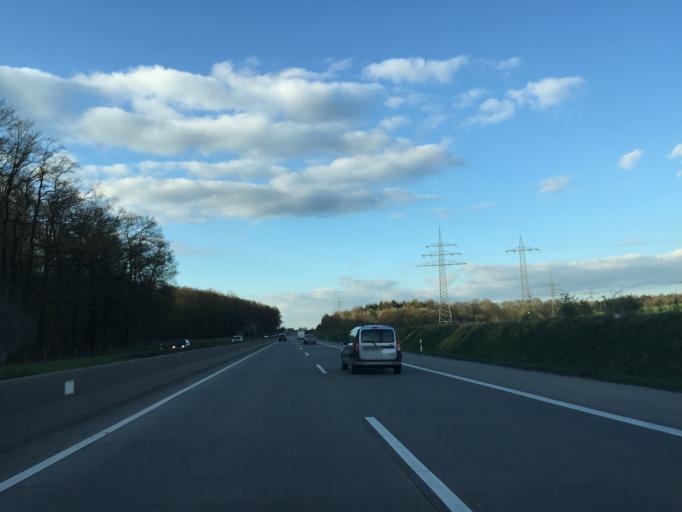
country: DE
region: Hesse
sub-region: Regierungsbezirk Giessen
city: Grossen Buseck
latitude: 50.5605
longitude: 8.7923
